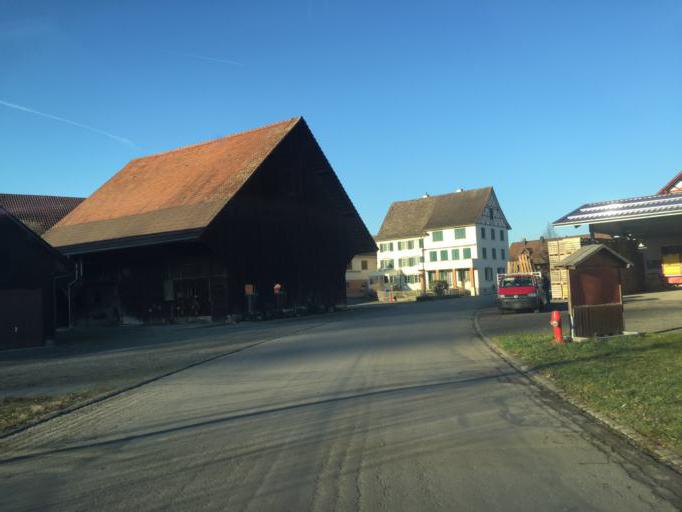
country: CH
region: Thurgau
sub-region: Frauenfeld District
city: Diessenhofen
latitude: 47.6632
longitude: 8.7678
